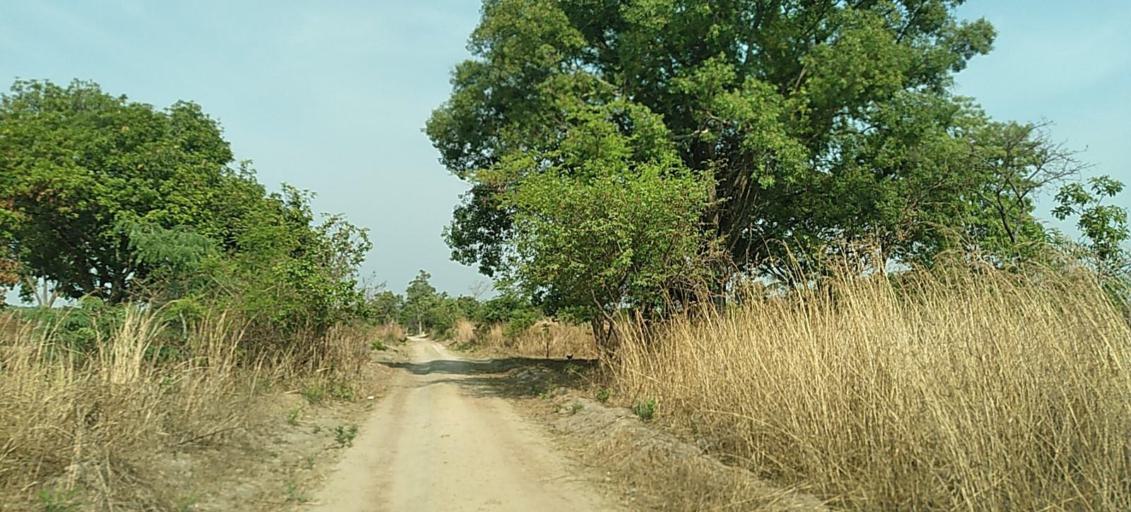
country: ZM
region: Copperbelt
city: Luanshya
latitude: -13.2184
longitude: 28.6553
